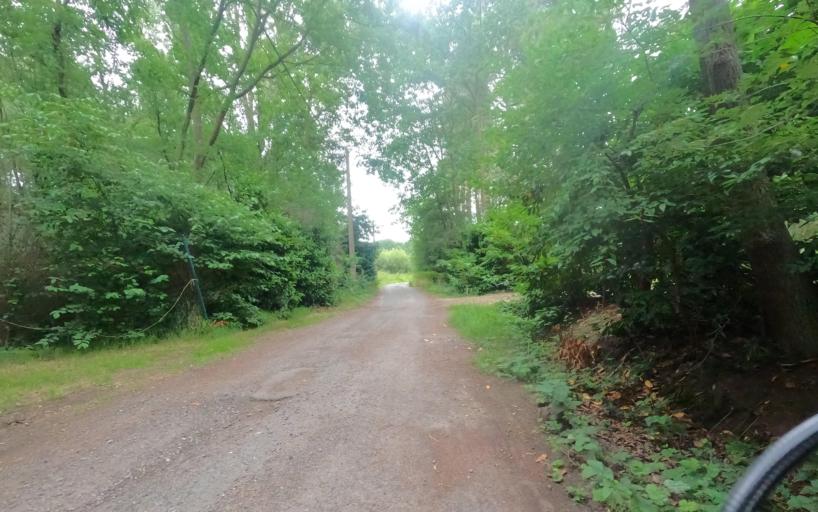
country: BE
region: Flanders
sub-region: Provincie Vlaams-Brabant
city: Rotselaar
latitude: 50.9783
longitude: 4.7423
